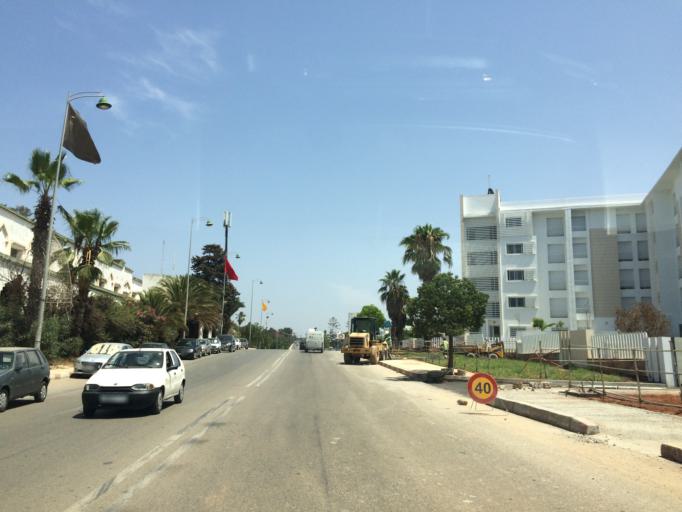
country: MA
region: Rabat-Sale-Zemmour-Zaer
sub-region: Skhirate-Temara
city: Temara
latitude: 33.9315
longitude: -6.9322
